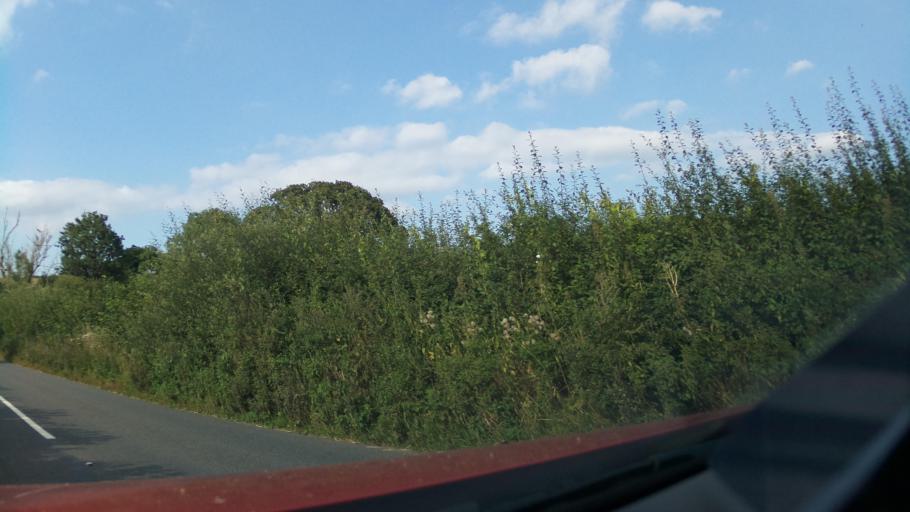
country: GB
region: England
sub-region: Devon
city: Tiverton
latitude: 50.8308
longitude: -3.4978
